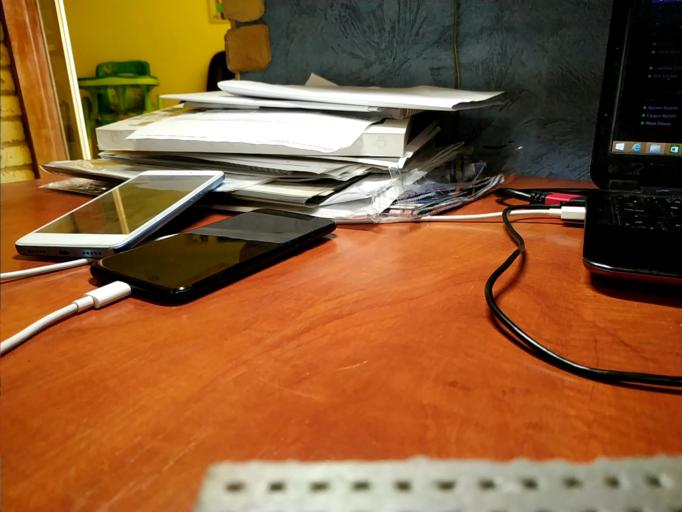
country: RU
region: Tverskaya
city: Spirovo
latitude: 57.4179
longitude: 35.1237
